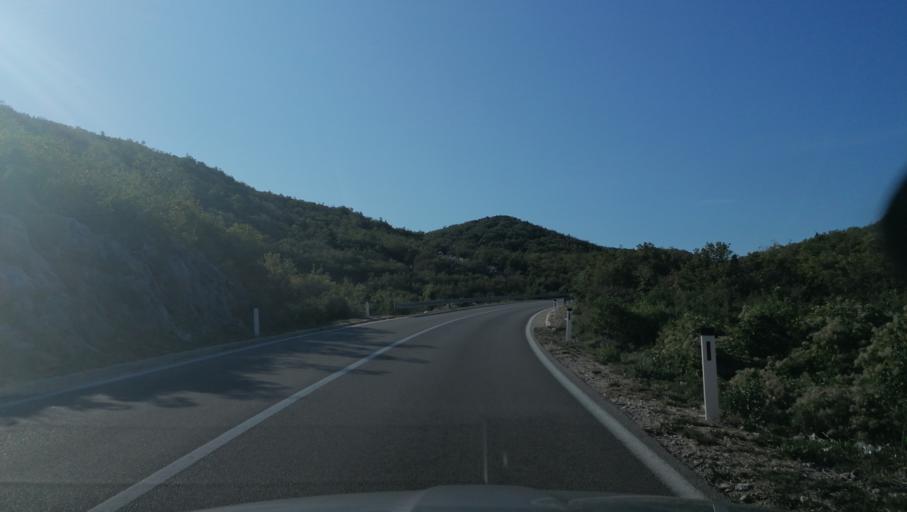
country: BA
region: Republika Srpska
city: Trebinje
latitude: 42.6579
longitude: 18.3660
